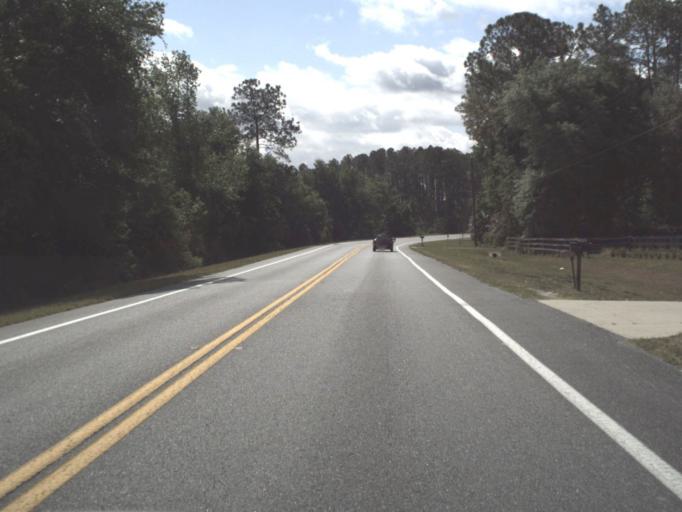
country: US
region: Florida
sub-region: Marion County
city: Ocala
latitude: 29.2265
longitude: -82.0367
